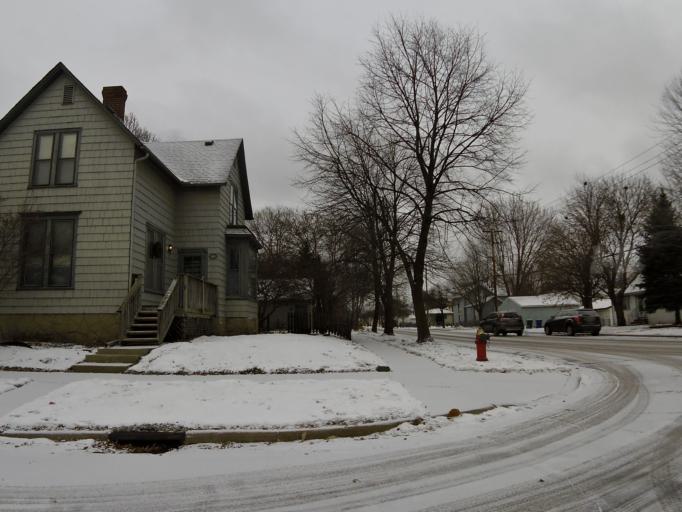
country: US
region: Minnesota
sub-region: Dakota County
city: West Saint Paul
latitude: 44.9224
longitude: -93.1366
